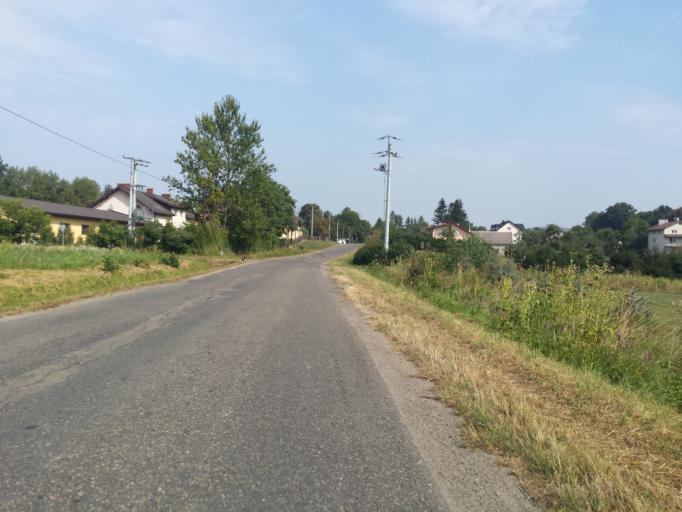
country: PL
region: Subcarpathian Voivodeship
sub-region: Powiat sanocki
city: Sanok
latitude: 49.6304
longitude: 22.2771
